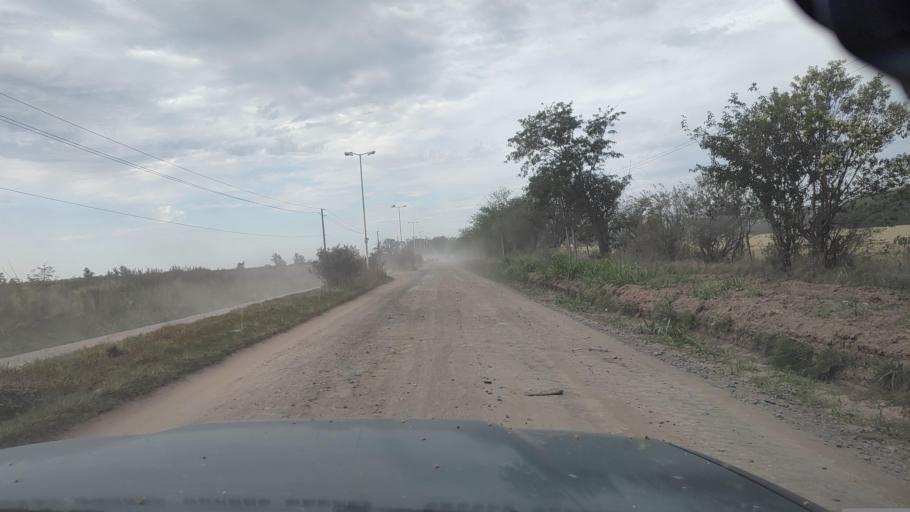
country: AR
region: Buenos Aires
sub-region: Partido de Lujan
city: Lujan
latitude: -34.5497
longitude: -59.0862
